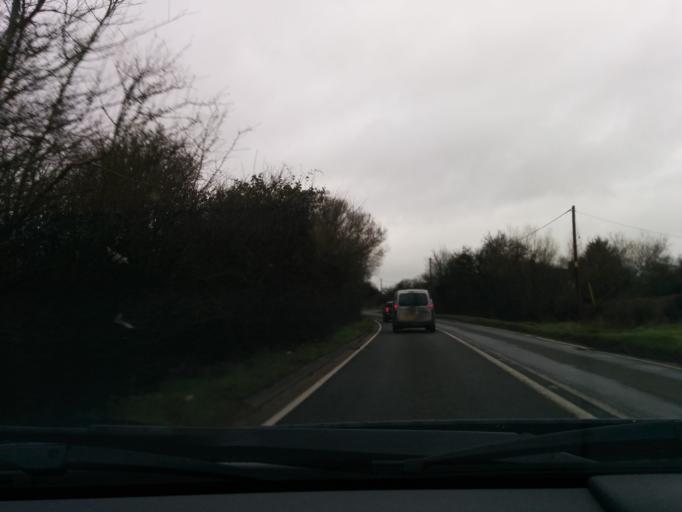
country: GB
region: England
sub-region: Oxfordshire
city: Eynsham
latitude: 51.7707
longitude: -1.3574
